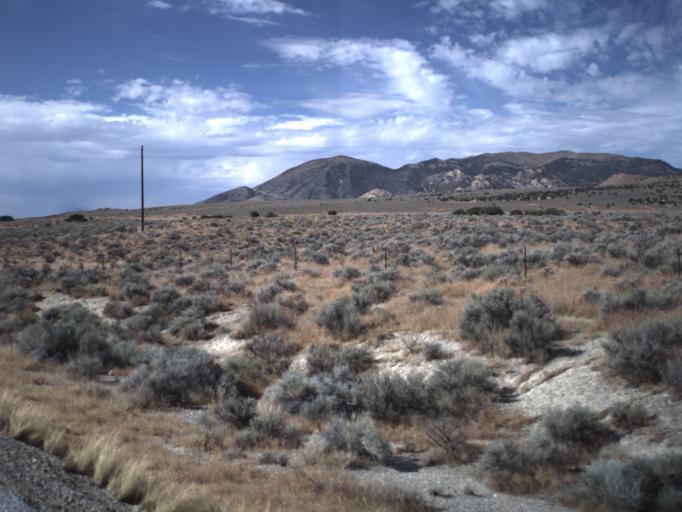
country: US
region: Utah
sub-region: Tooele County
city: Wendover
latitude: 41.5275
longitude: -113.5950
